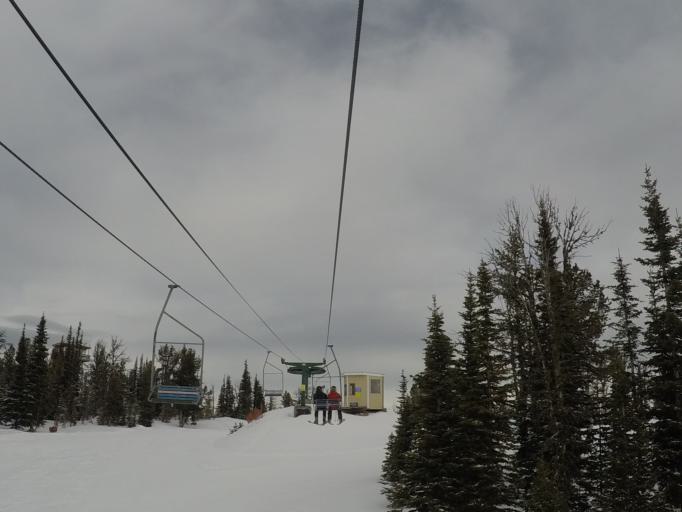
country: US
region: Montana
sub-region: Meagher County
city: White Sulphur Springs
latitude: 46.8379
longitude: -110.7165
